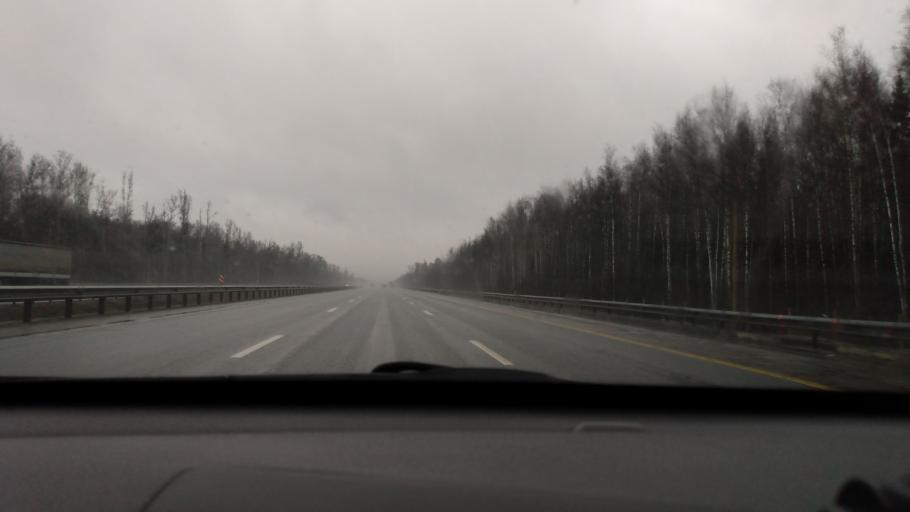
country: RU
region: Moskovskaya
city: Zhilevo
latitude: 54.9376
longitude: 37.9920
